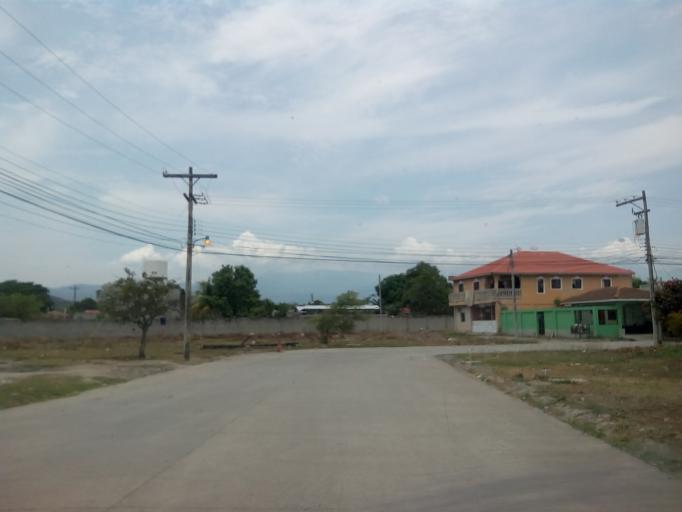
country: HN
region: Cortes
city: La Lima
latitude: 15.4606
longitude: -87.9485
